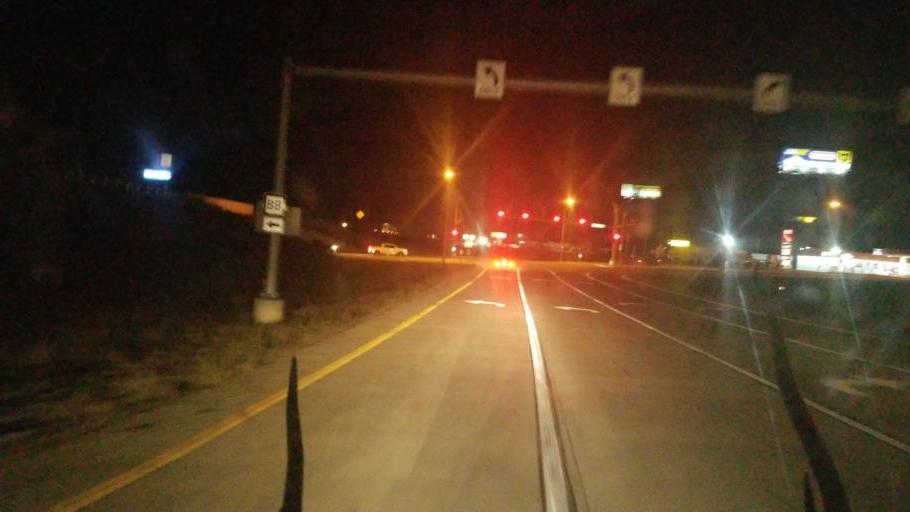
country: US
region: Missouri
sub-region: Jackson County
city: Grain Valley
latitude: 39.0211
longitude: -94.1992
